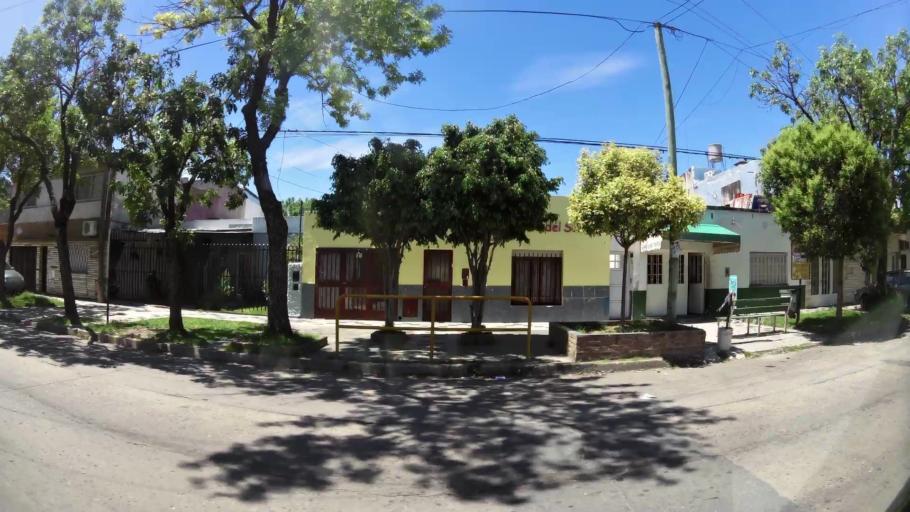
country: AR
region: Santa Fe
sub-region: Departamento de Rosario
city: Rosario
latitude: -32.9430
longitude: -60.7086
